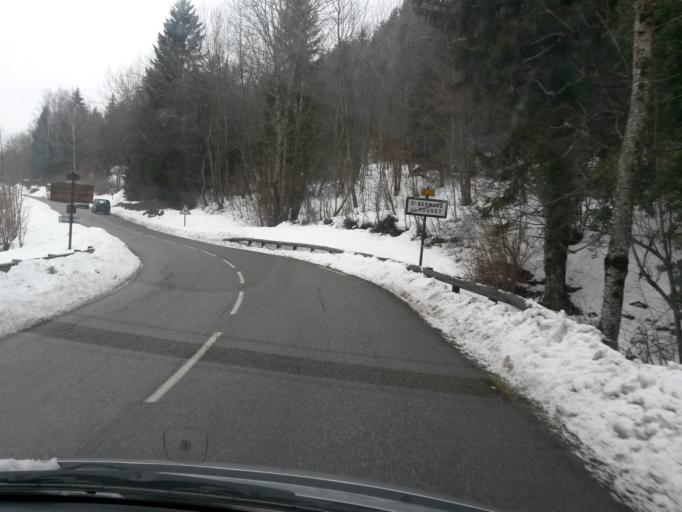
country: FR
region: Rhone-Alpes
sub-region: Departement de l'Isere
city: Lumbin
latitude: 45.3243
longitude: 5.8957
